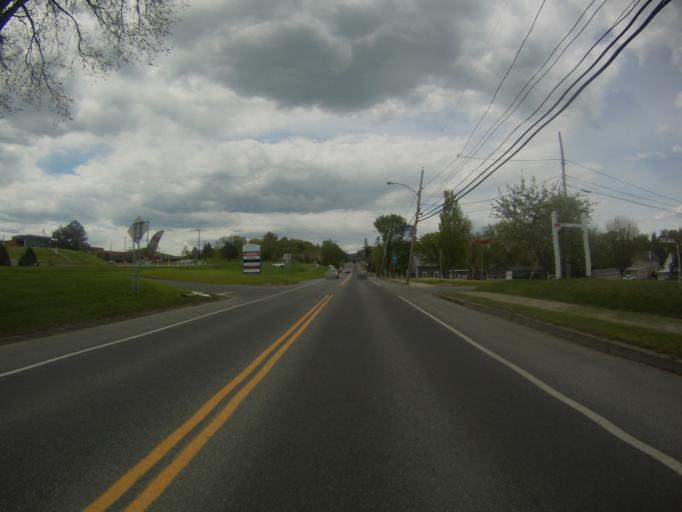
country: US
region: New York
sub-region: Essex County
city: Ticonderoga
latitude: 43.8490
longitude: -73.4352
